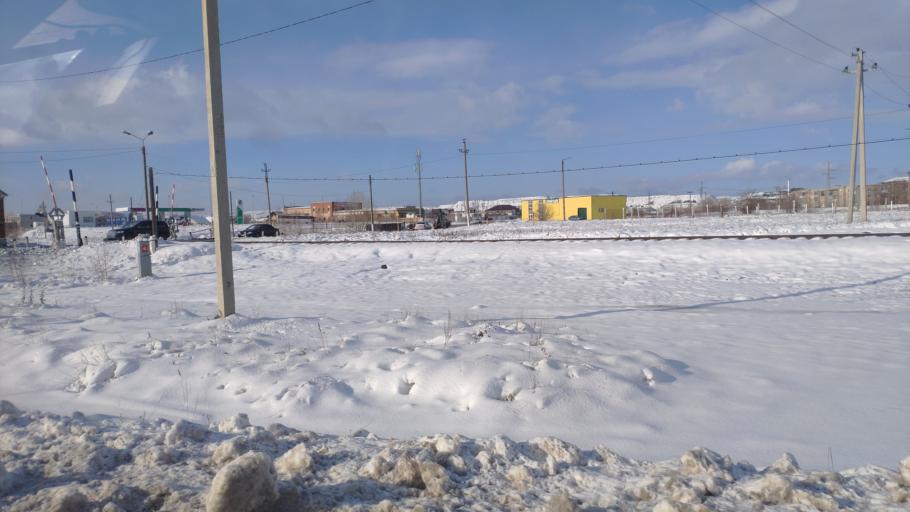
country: RU
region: Bashkortostan
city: Sibay
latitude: 52.7041
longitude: 58.6641
